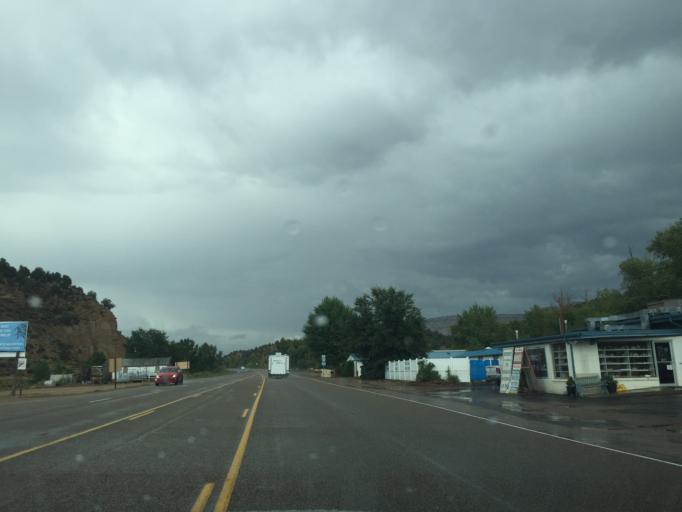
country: US
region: Utah
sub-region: Kane County
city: Kanab
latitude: 37.2240
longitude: -112.6804
